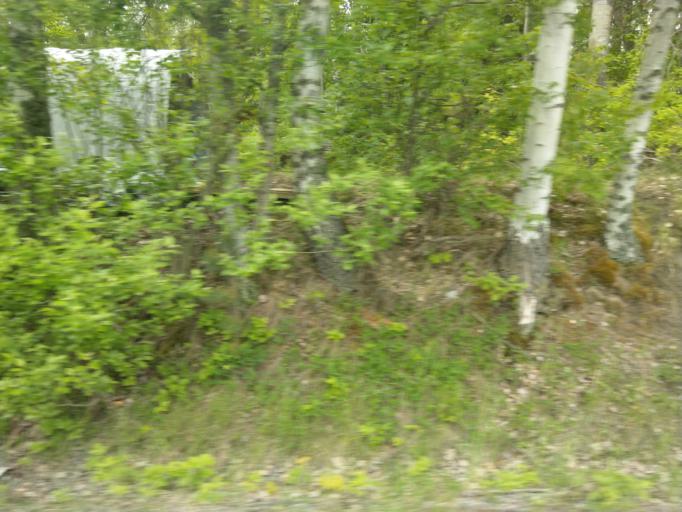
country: SE
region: Stockholm
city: Stenhamra
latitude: 59.4080
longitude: 17.6239
